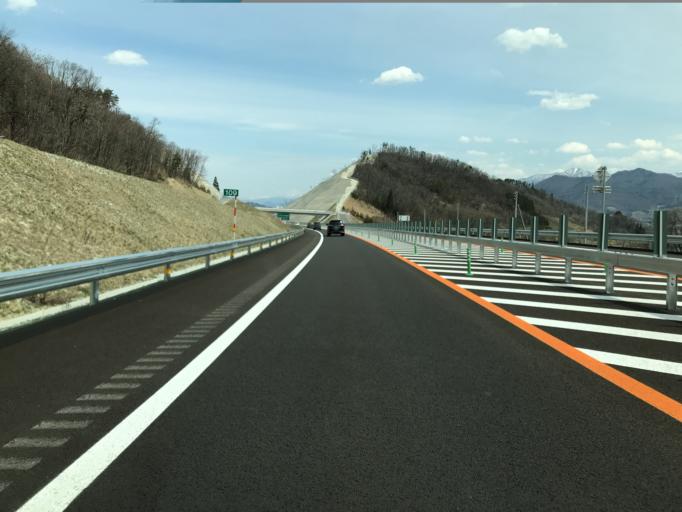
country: JP
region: Yamagata
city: Kaminoyama
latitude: 38.1156
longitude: 140.2464
